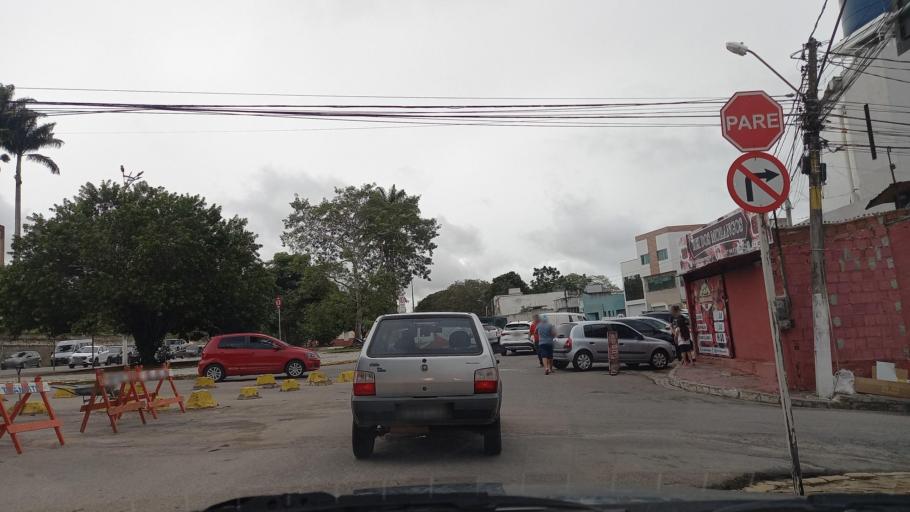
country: BR
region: Pernambuco
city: Garanhuns
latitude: -8.8887
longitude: -36.4951
